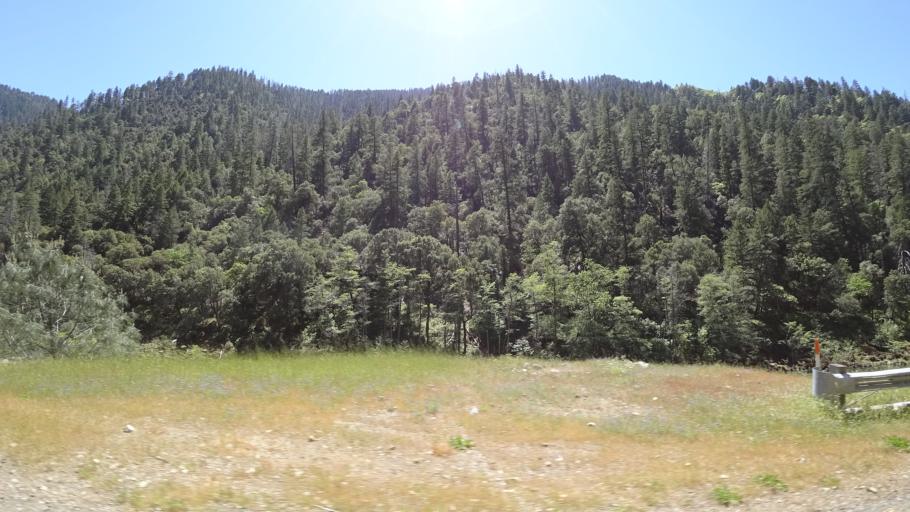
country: US
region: California
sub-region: Humboldt County
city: Willow Creek
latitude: 40.7955
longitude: -123.3790
